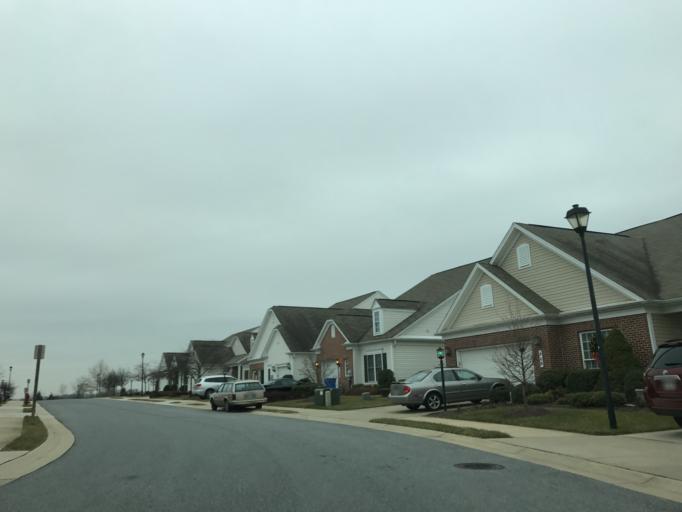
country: US
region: Maryland
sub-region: Carroll County
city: Taneytown
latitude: 39.6436
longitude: -77.1591
